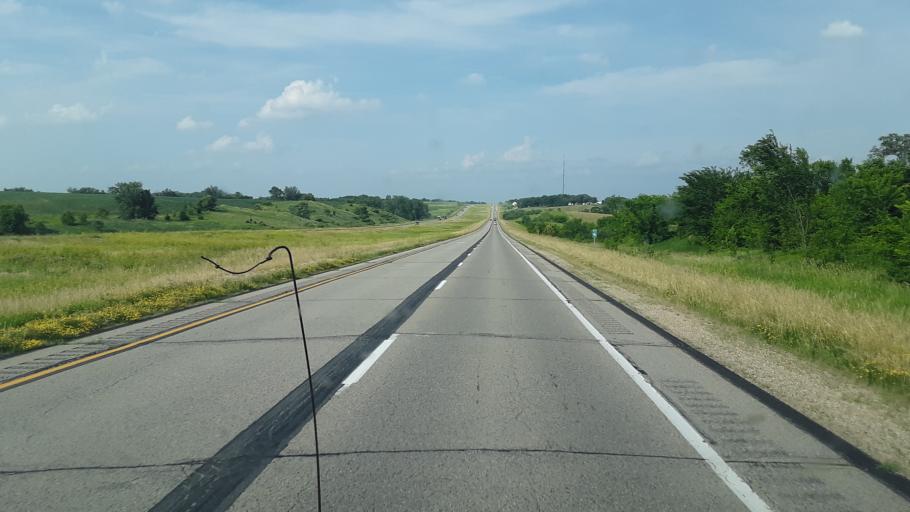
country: US
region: Iowa
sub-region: Jasper County
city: Baxter
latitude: 41.8679
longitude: -93.2252
